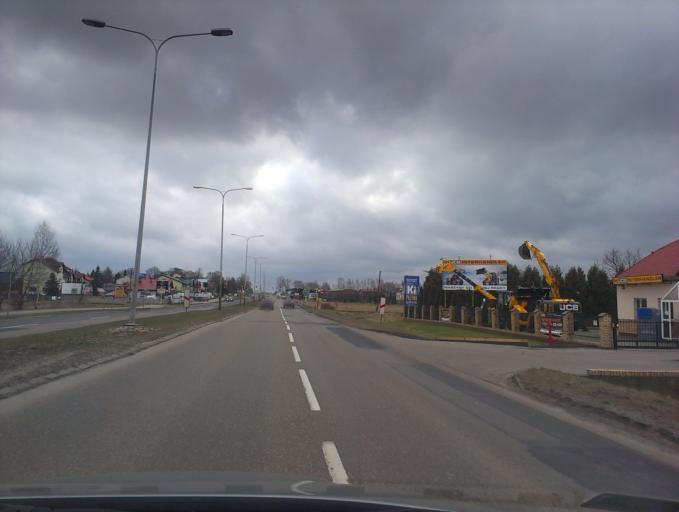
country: PL
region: West Pomeranian Voivodeship
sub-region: Koszalin
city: Koszalin
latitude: 54.1658
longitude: 16.2143
